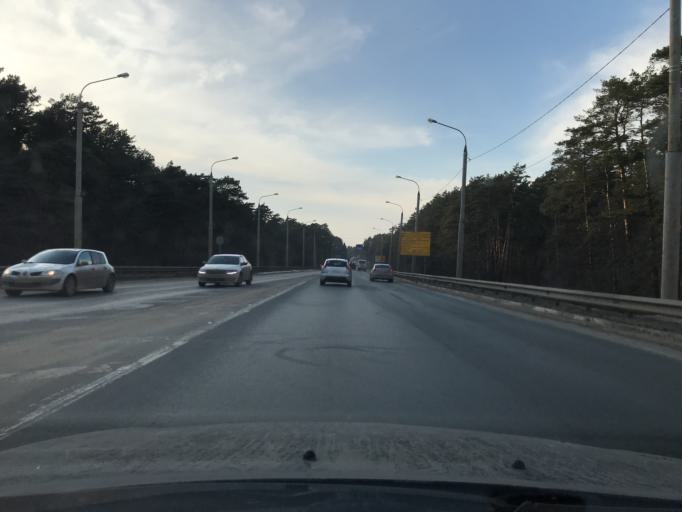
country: RU
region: Kaluga
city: Kaluga
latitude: 54.5141
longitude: 36.2081
